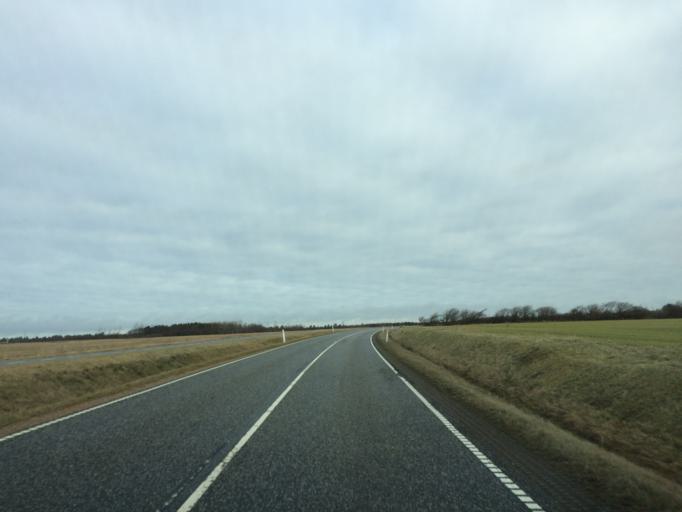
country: DK
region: Central Jutland
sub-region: Holstebro Kommune
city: Ulfborg
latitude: 56.3574
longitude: 8.3814
